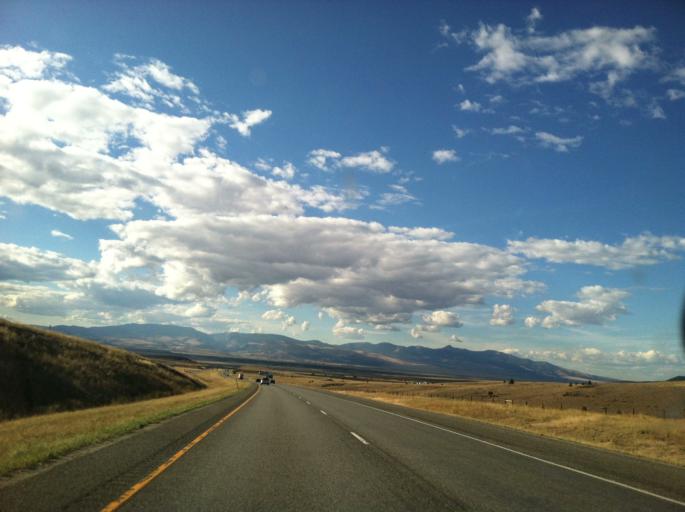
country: US
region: Montana
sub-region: Deer Lodge County
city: Warm Springs
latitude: 46.0441
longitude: -112.7420
